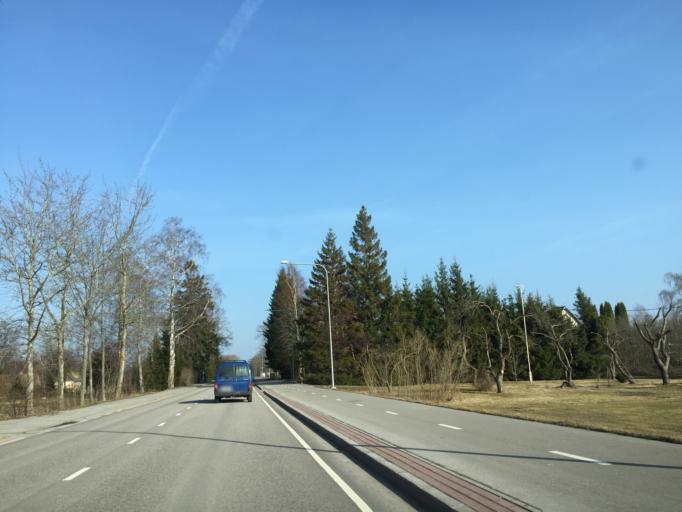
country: EE
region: Saare
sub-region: Kuressaare linn
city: Kuressaare
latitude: 58.2287
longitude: 22.3894
